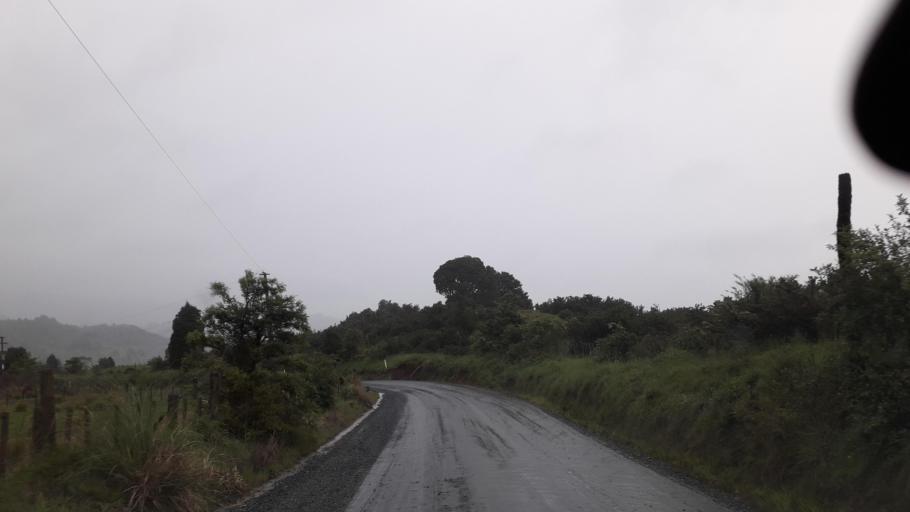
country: NZ
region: Northland
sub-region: Far North District
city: Kerikeri
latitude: -35.1231
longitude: 173.7472
